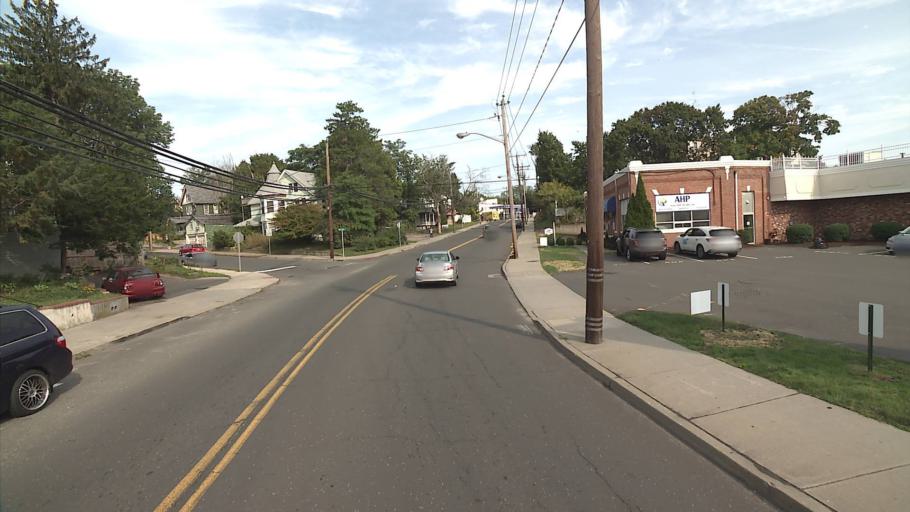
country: US
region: Connecticut
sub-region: Fairfield County
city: Norwalk
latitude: 41.1228
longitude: -73.4155
